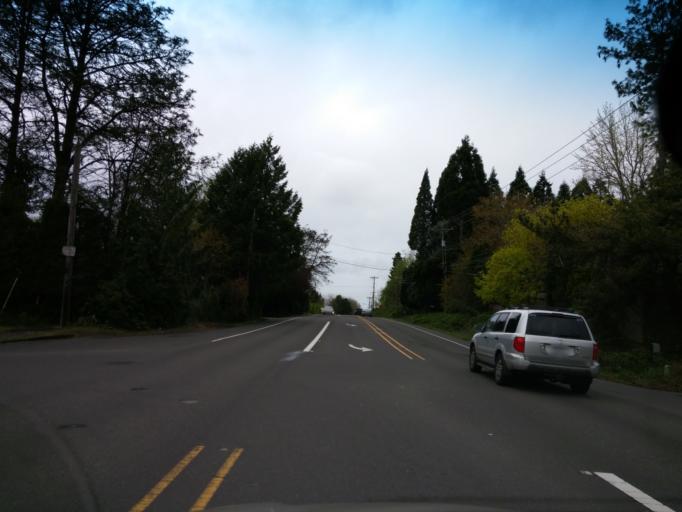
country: US
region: Oregon
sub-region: Washington County
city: Oak Hills
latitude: 45.5244
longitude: -122.8597
